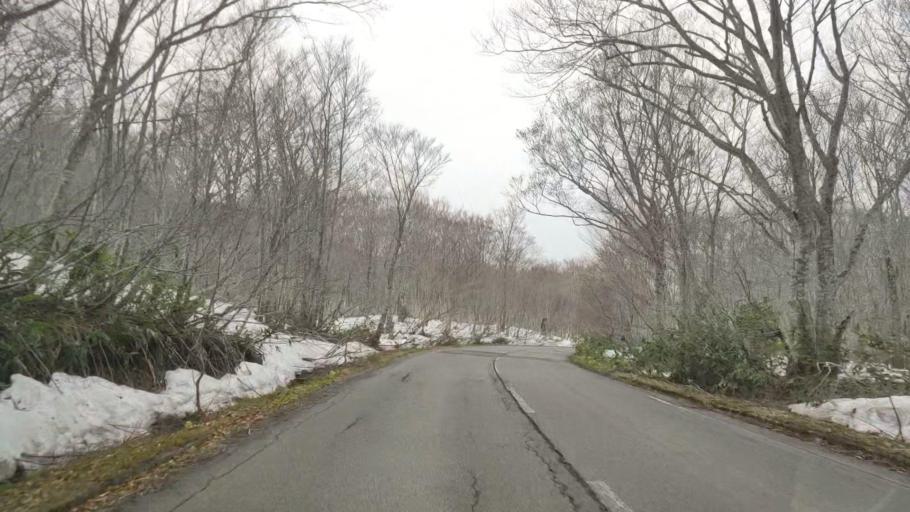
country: JP
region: Aomori
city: Aomori Shi
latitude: 40.6511
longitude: 140.9467
